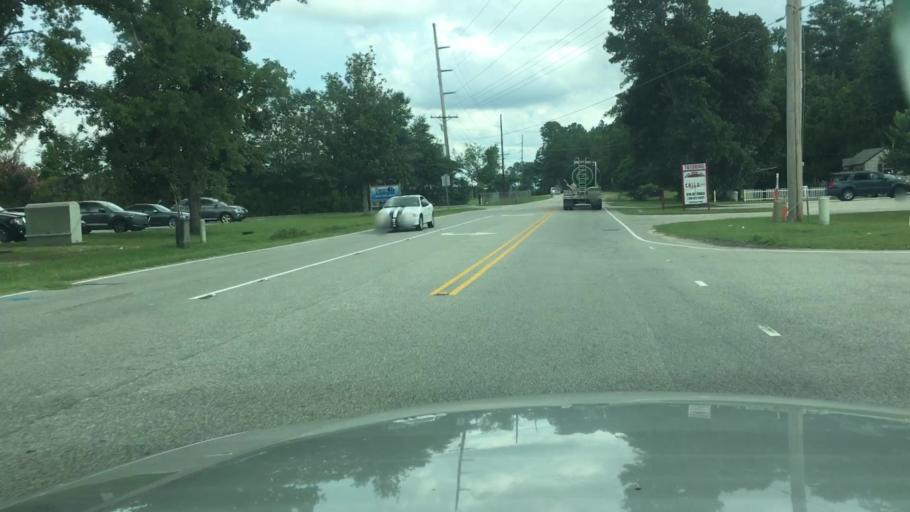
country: US
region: North Carolina
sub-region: Cumberland County
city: Hope Mills
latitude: 35.0056
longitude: -78.9977
